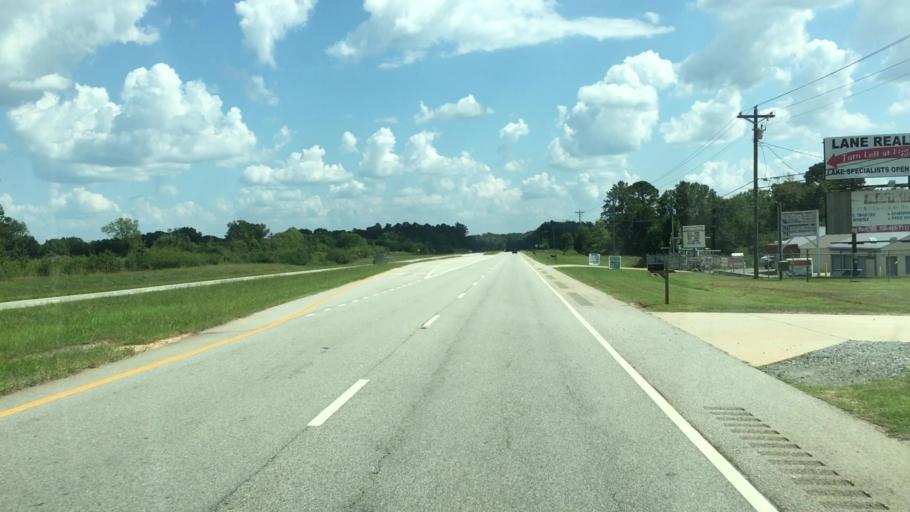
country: US
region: Georgia
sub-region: Putnam County
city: Eatonton
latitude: 33.2515
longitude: -83.3277
